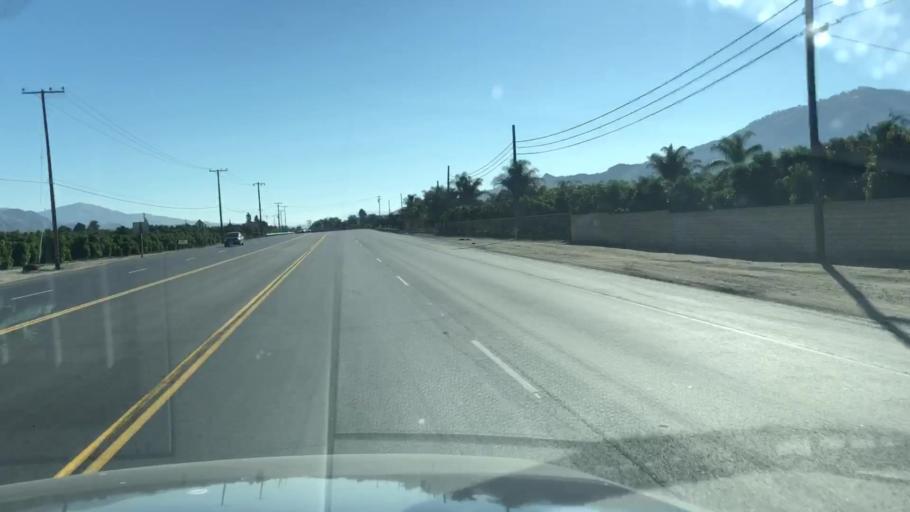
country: US
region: California
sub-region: Ventura County
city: Piru
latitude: 34.4007
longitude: -118.8137
